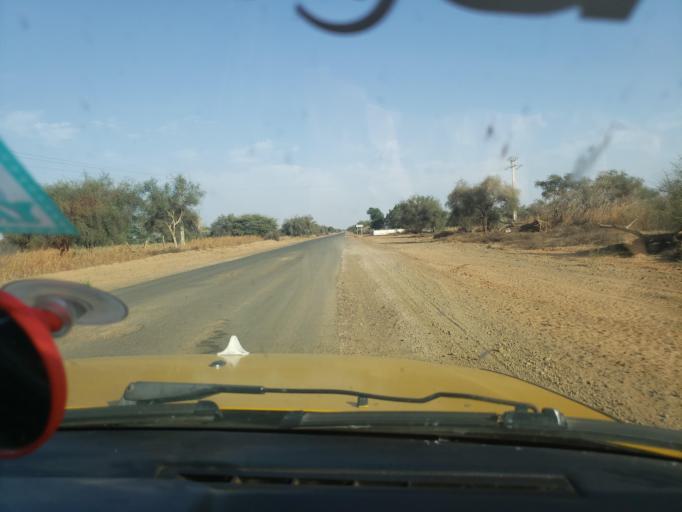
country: SN
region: Louga
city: Louga
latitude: 15.5031
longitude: -15.9484
